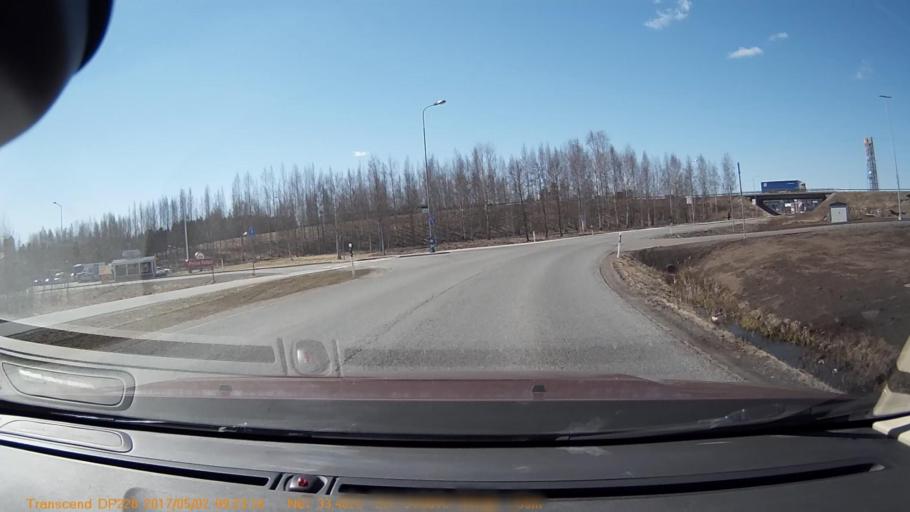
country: FI
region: Pirkanmaa
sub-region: Tampere
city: Yloejaervi
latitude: 61.5566
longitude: 23.5790
